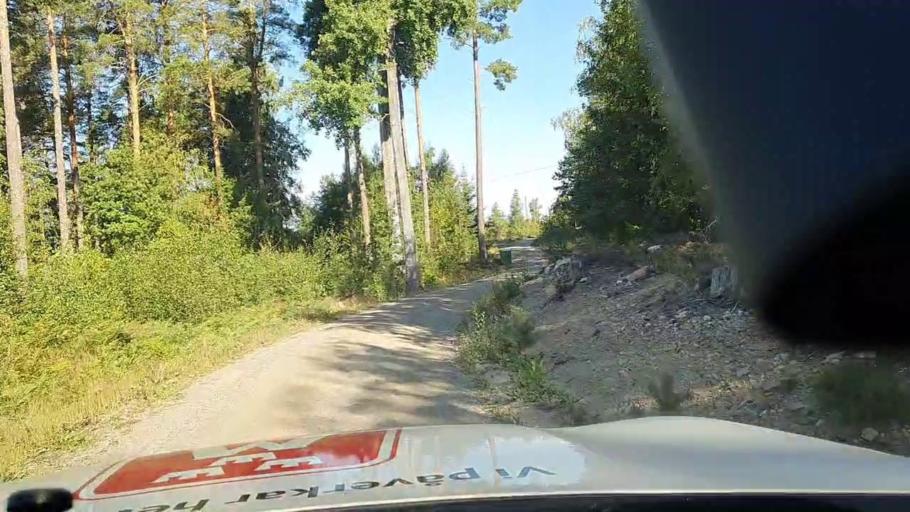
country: SE
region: Soedermanland
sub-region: Eskilstuna Kommun
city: Eskilstuna
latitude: 59.4586
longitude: 16.6497
